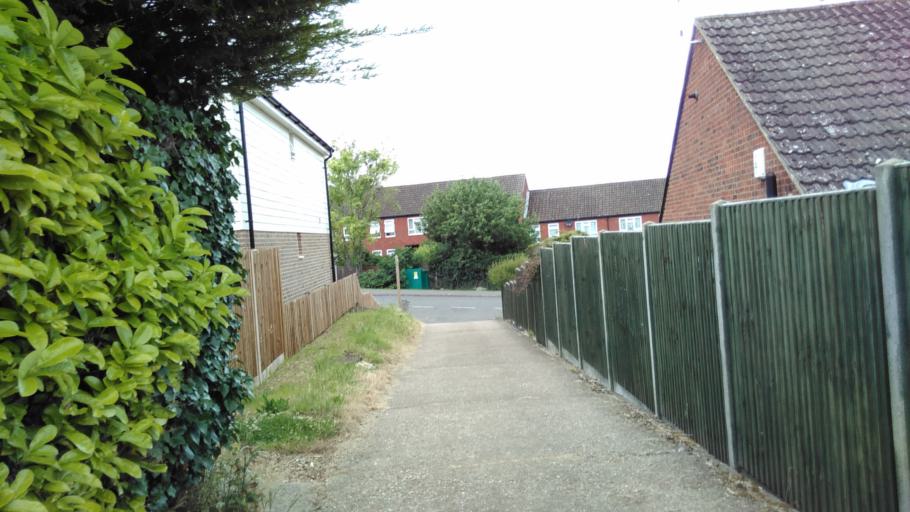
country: GB
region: England
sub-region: Kent
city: Chartham
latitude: 51.2538
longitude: 1.0089
